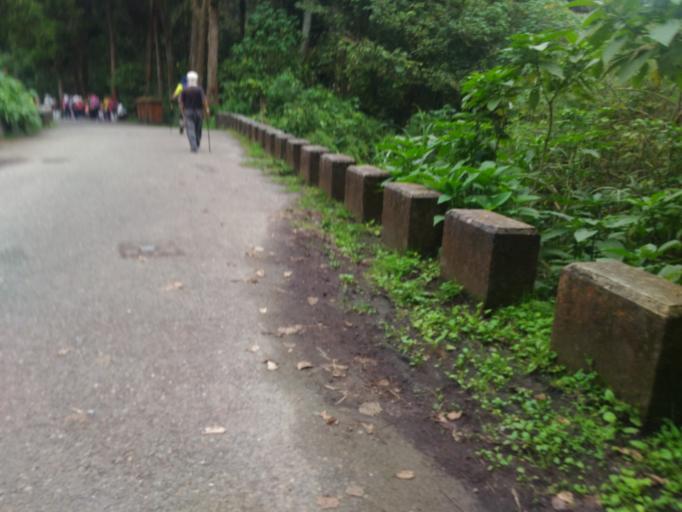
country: TW
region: Taiwan
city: Lugu
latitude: 23.6661
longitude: 120.7929
